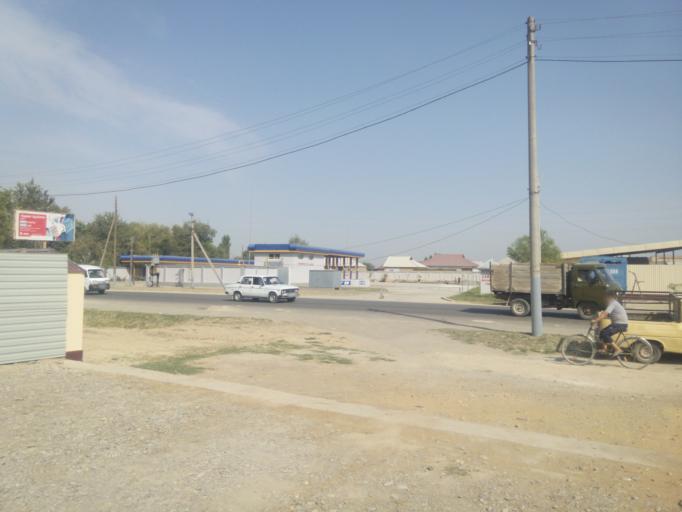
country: UZ
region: Sirdaryo
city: Guliston
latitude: 40.4942
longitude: 68.7974
